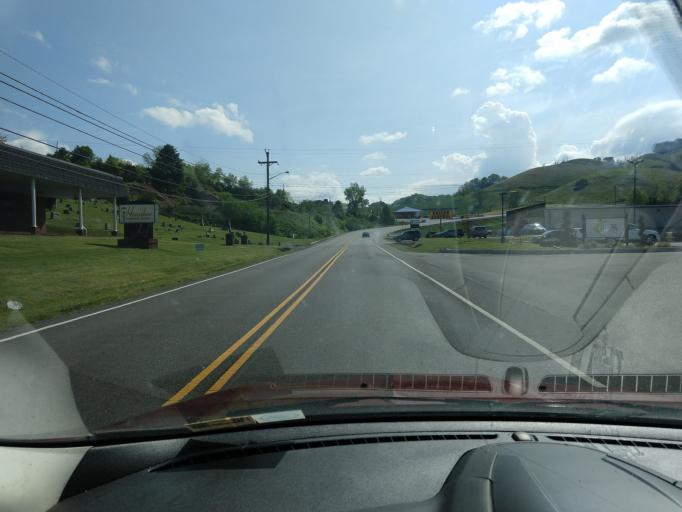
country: US
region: Virginia
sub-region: Russell County
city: Honaker
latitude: 37.0155
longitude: -81.9596
